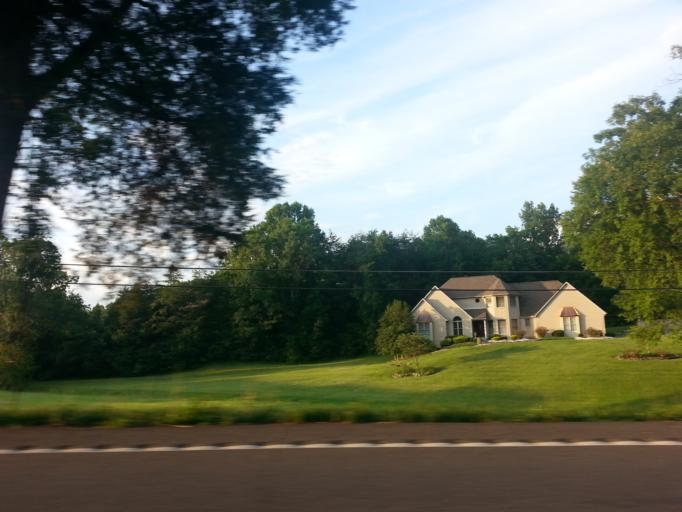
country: US
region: Tennessee
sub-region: Anderson County
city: Norris
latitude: 36.1261
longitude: -83.9965
